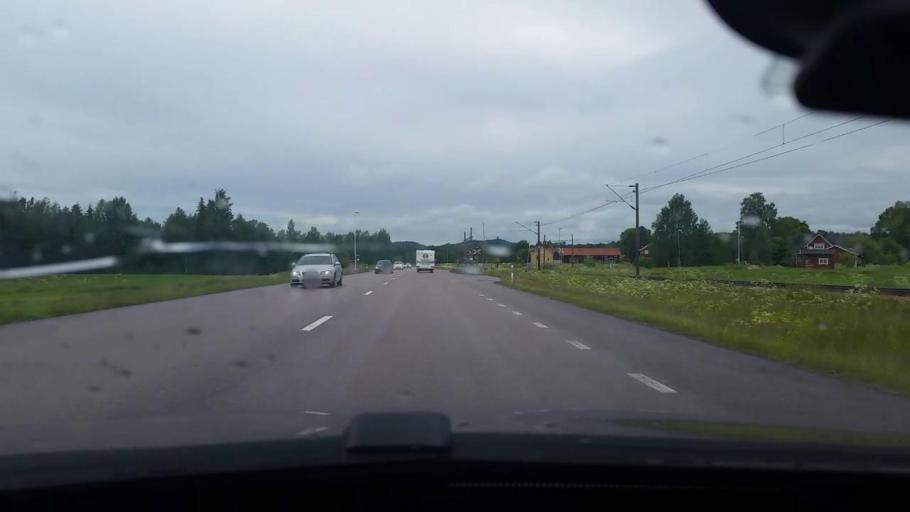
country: SE
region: Dalarna
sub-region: Gagnefs Kommun
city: Djuras
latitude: 60.5736
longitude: 15.1239
